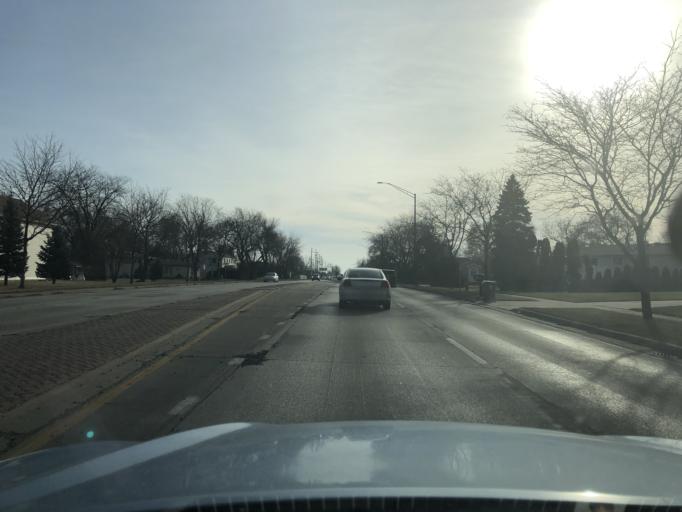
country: US
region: Illinois
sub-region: DuPage County
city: Roselle
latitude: 42.0039
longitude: -88.0801
